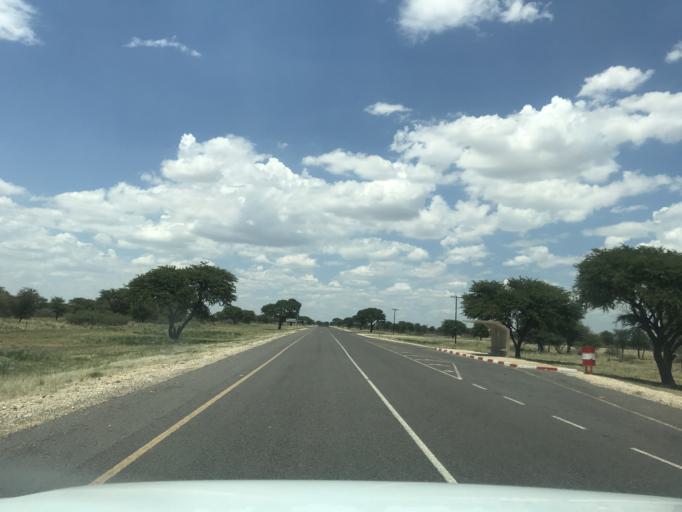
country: BW
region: South East
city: Janeng
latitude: -25.6398
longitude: 25.1514
